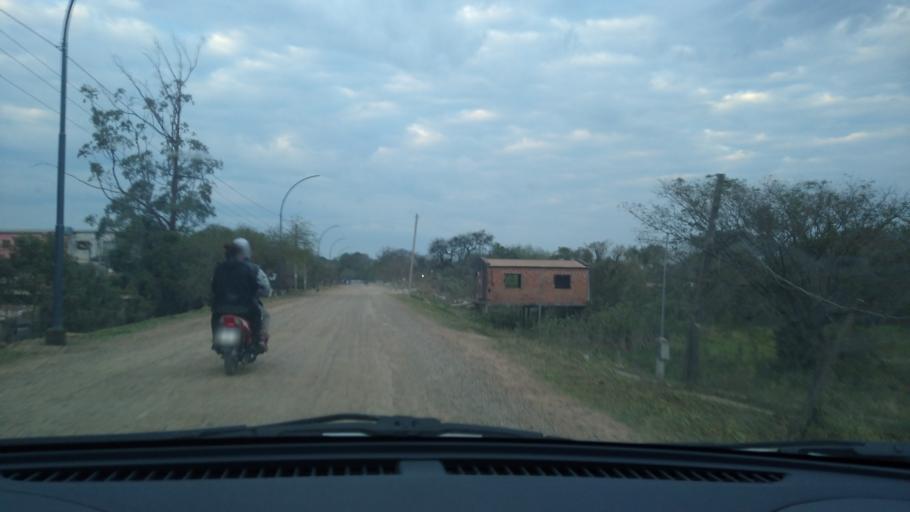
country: AR
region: Chaco
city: Barranqueras
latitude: -27.4611
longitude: -58.9509
